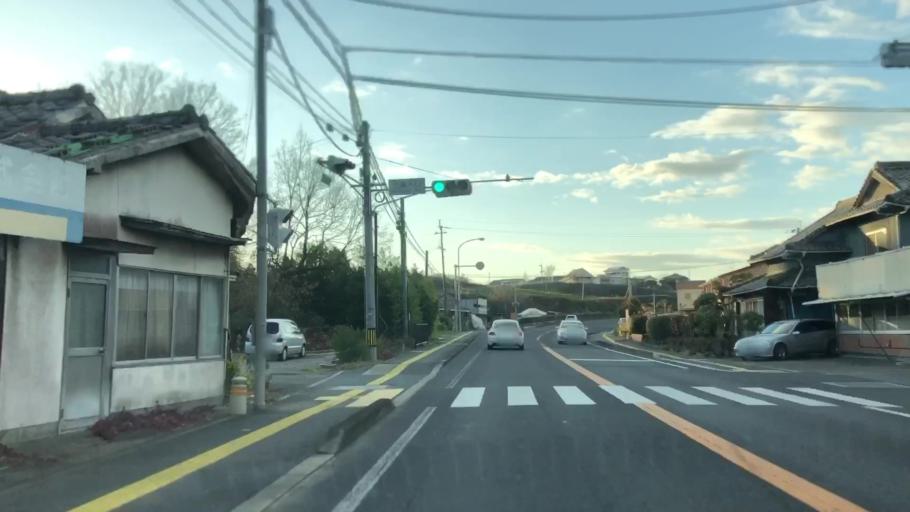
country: JP
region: Oita
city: Bungo-Takada-shi
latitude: 33.5351
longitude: 131.3148
